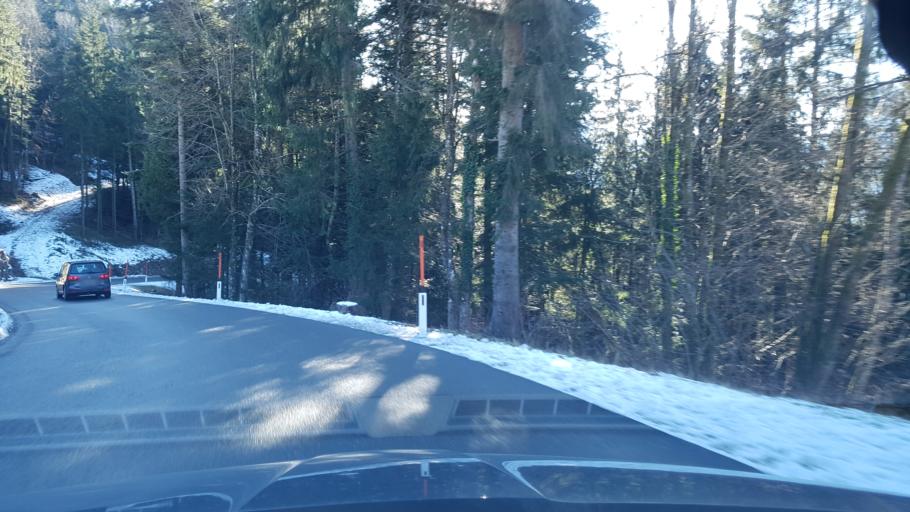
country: AT
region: Salzburg
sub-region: Politischer Bezirk Hallein
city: Golling an der Salzach
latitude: 47.6250
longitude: 13.1866
